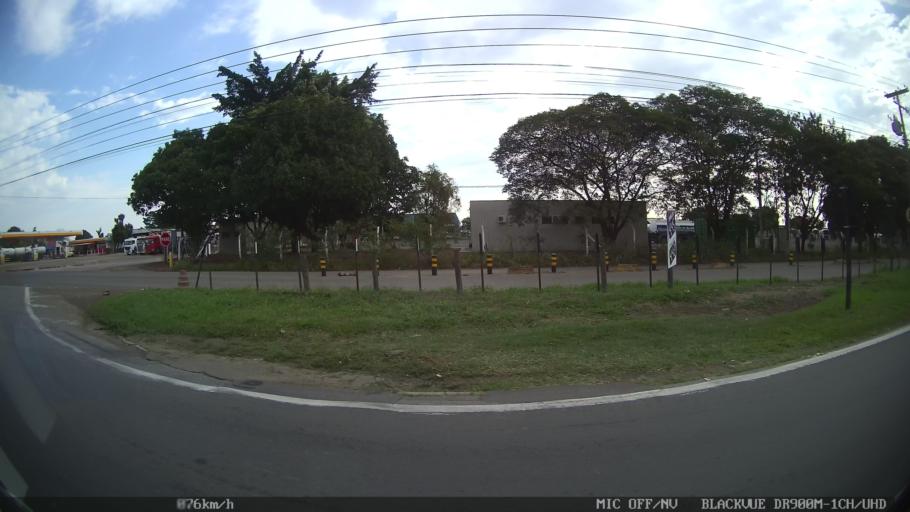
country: BR
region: Sao Paulo
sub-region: Paulinia
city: Paulinia
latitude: -22.7188
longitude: -47.1430
